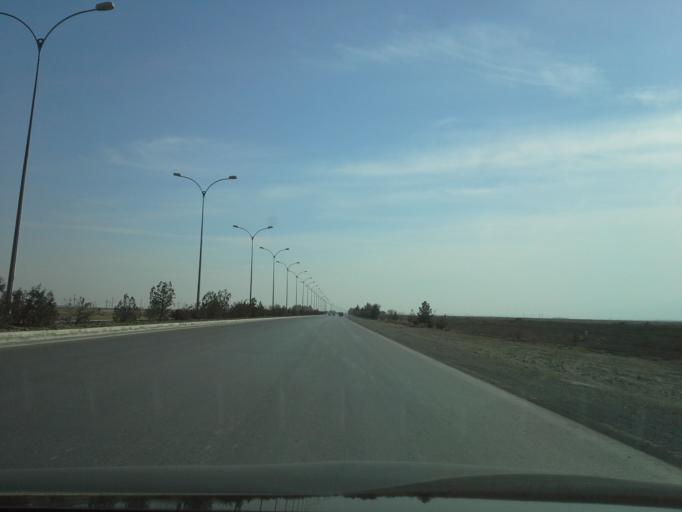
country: TM
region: Ahal
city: Abadan
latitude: 38.1281
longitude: 58.0279
